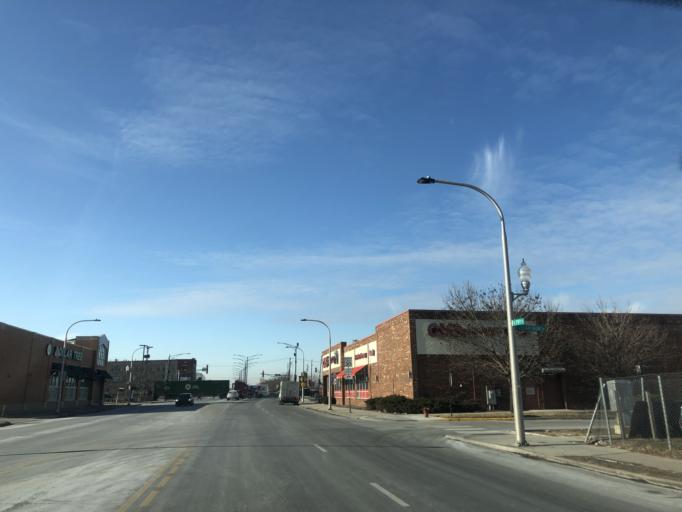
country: US
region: Illinois
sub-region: Cook County
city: Evergreen Park
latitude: 41.7501
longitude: -87.6811
